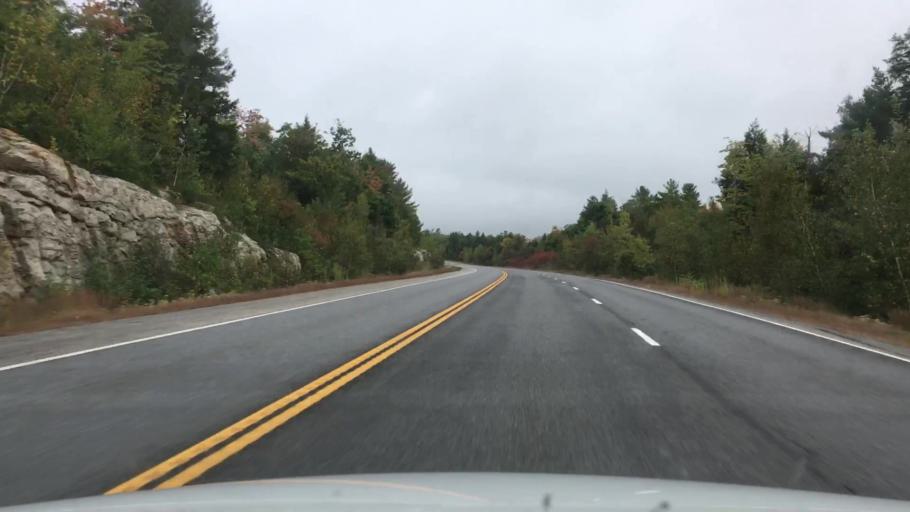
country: US
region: Maine
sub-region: Cumberland County
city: New Gloucester
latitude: 43.9534
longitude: -70.3509
